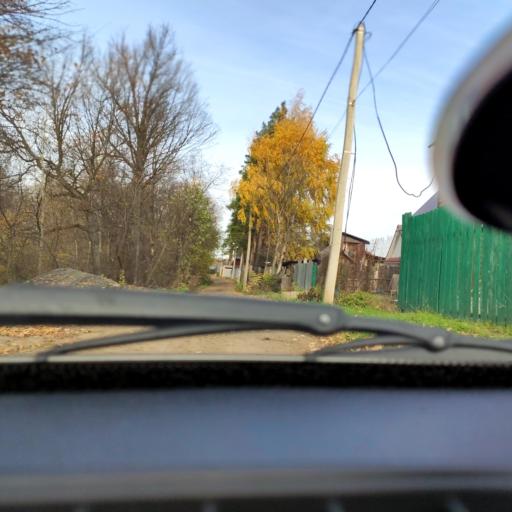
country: RU
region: Bashkortostan
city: Ufa
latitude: 54.7878
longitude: 55.9436
